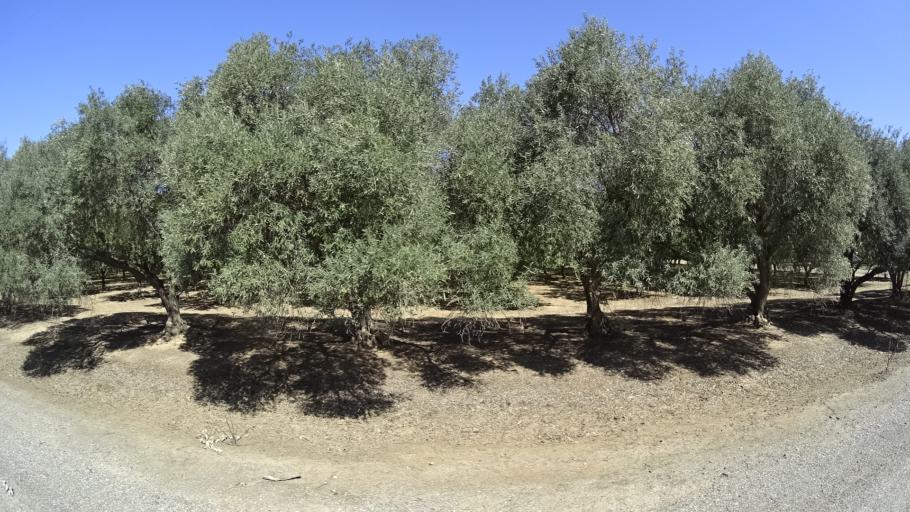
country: US
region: California
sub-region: Glenn County
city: Hamilton City
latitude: 39.7755
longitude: -122.0347
